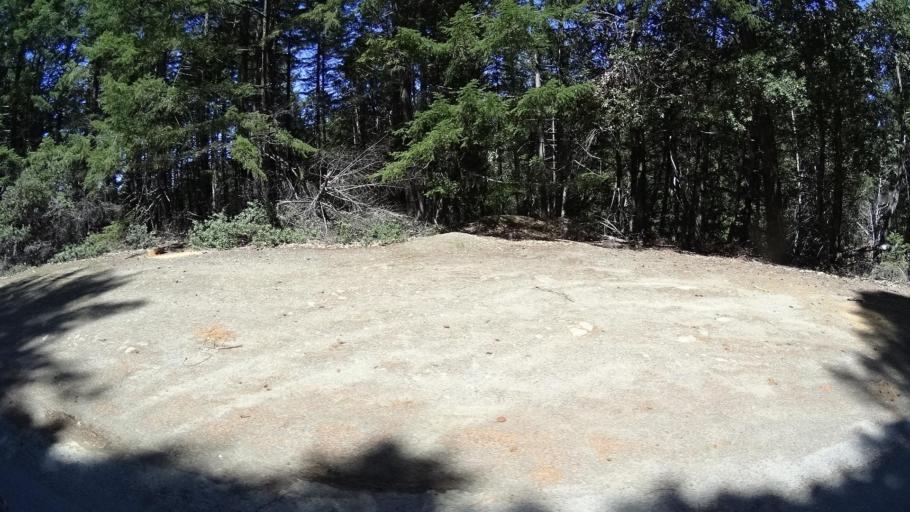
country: US
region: California
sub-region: Humboldt County
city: Rio Dell
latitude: 40.2850
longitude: -124.0561
